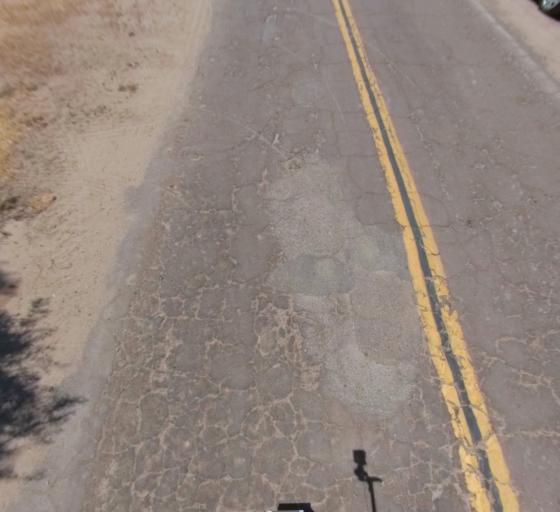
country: US
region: California
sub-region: Madera County
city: Parkwood
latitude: 36.8590
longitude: -120.0741
